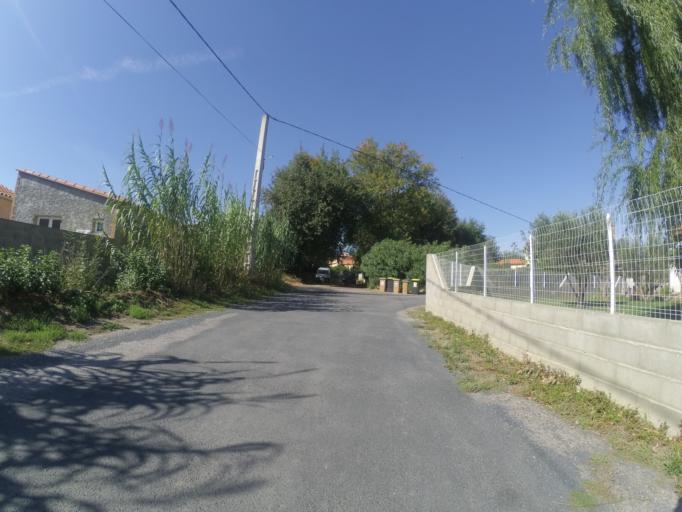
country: FR
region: Languedoc-Roussillon
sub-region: Departement des Pyrenees-Orientales
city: Pezilla-la-Riviere
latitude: 42.6915
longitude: 2.7659
